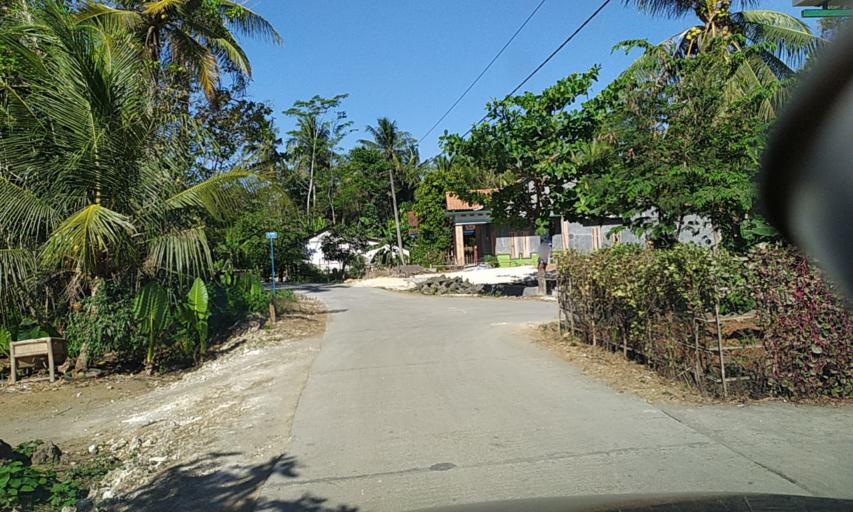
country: ID
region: Central Java
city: Kalenaren
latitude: -7.5829
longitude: 108.7944
